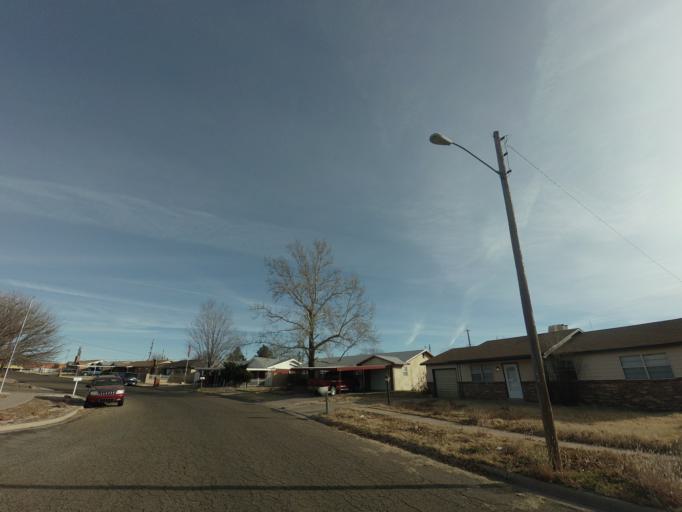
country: US
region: New Mexico
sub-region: Curry County
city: Clovis
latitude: 34.4180
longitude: -103.2202
